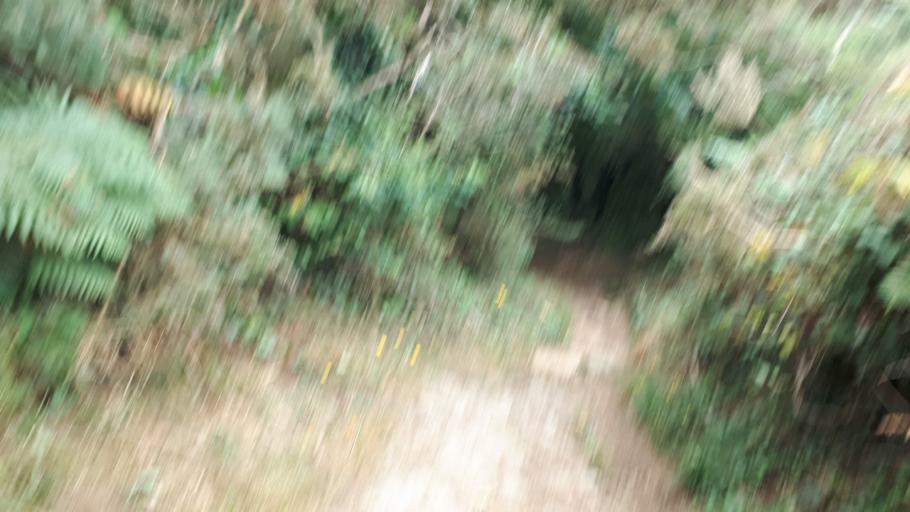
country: FR
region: Brittany
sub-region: Departement des Cotes-d'Armor
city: Plouha
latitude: 48.6988
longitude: -2.9052
